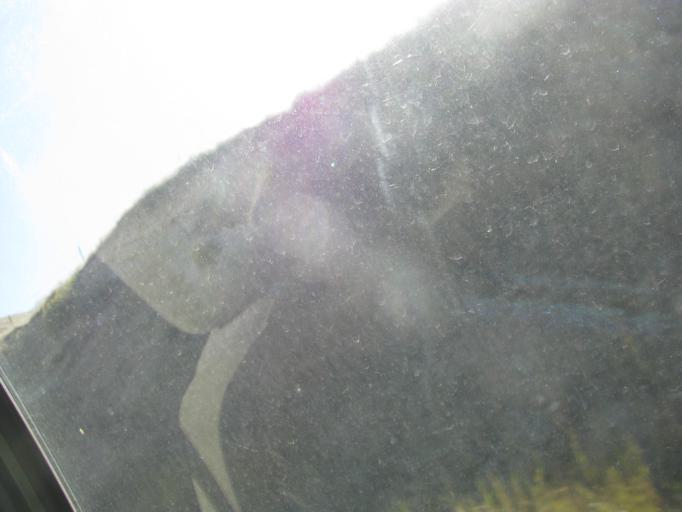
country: US
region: Washington
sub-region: Asotin County
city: Asotin
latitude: 46.3209
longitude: -117.0539
